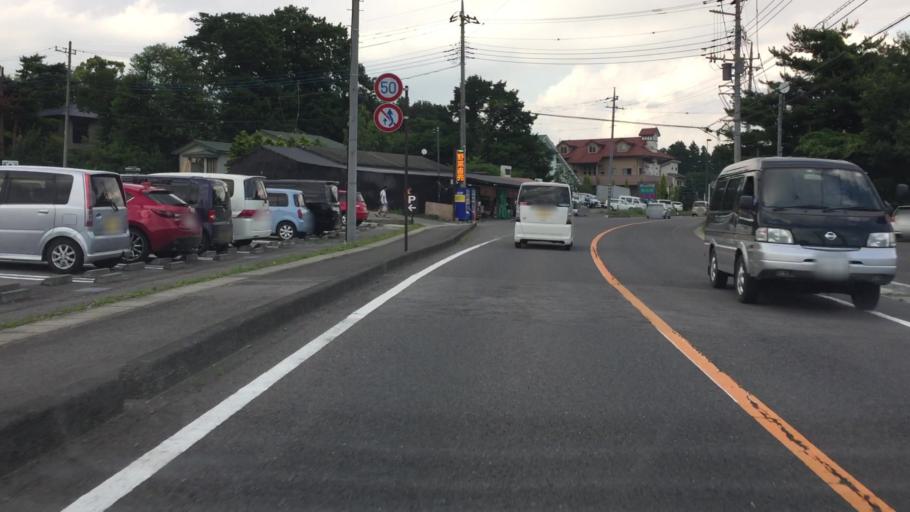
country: JP
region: Tochigi
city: Kuroiso
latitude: 37.0513
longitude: 140.0321
